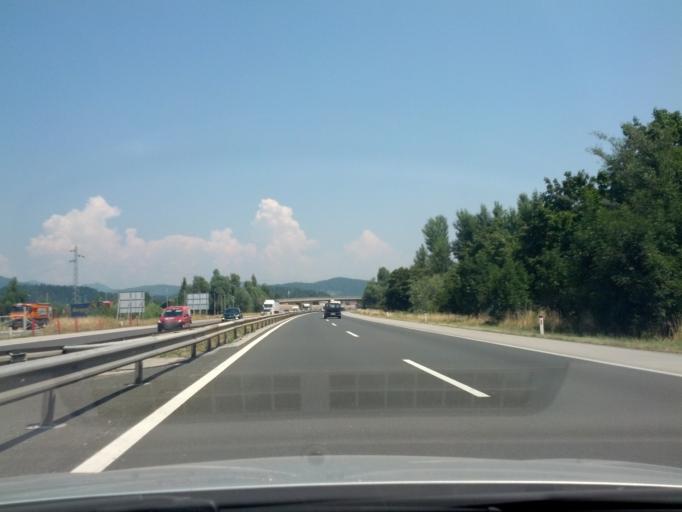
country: SI
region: Vrhnika
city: Vrhnika
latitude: 45.9747
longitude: 14.3075
